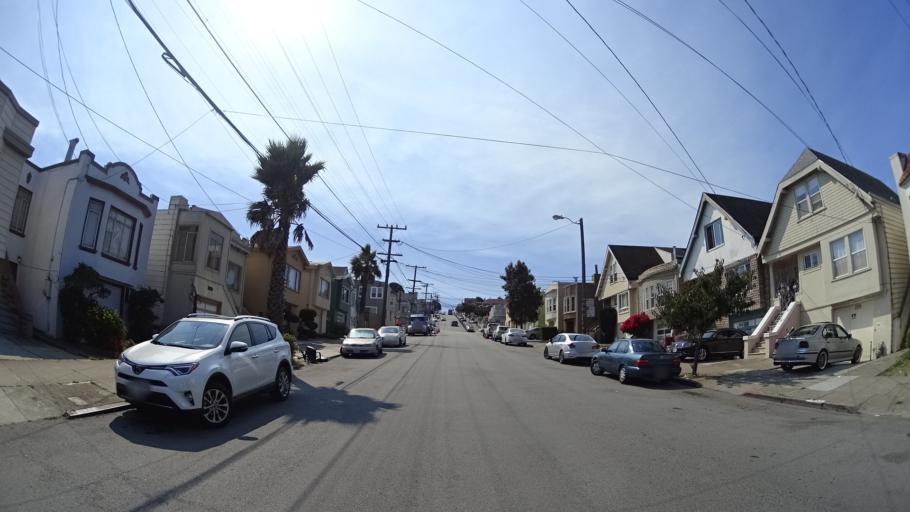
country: US
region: California
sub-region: San Mateo County
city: Daly City
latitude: 37.7209
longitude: -122.4561
